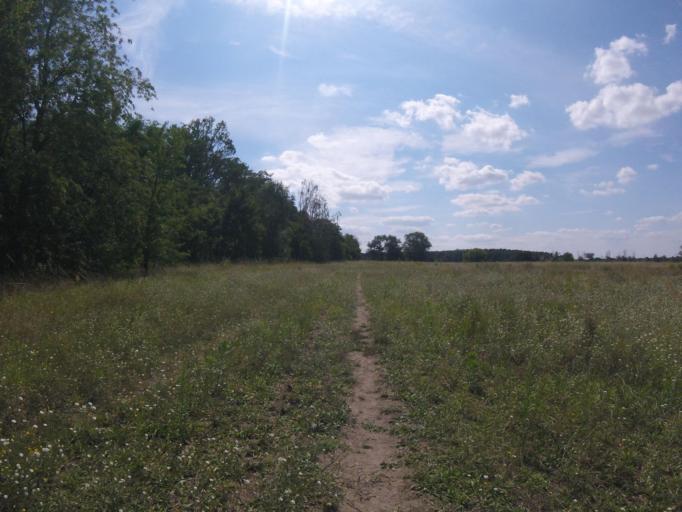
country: DE
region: Brandenburg
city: Wildau
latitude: 52.3259
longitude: 13.6084
